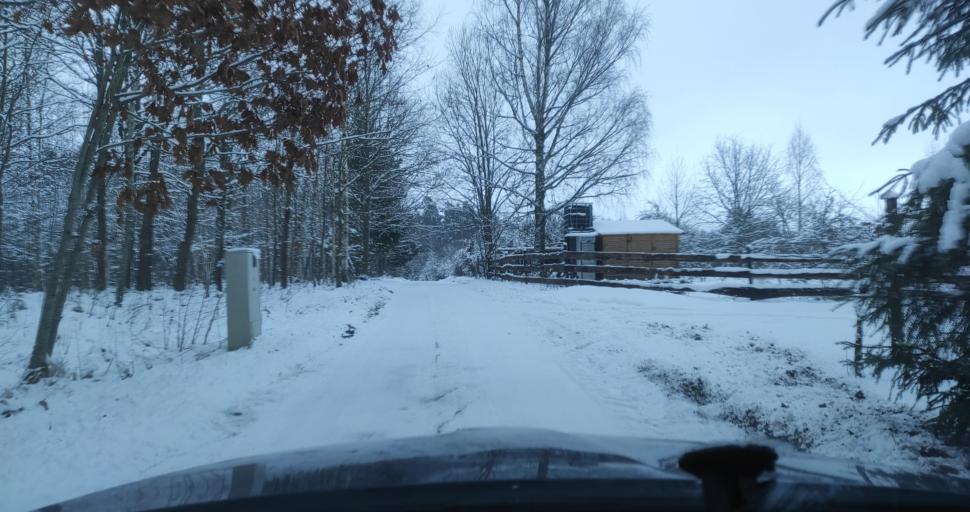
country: LV
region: Kuldigas Rajons
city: Kuldiga
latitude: 56.9916
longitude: 22.0443
